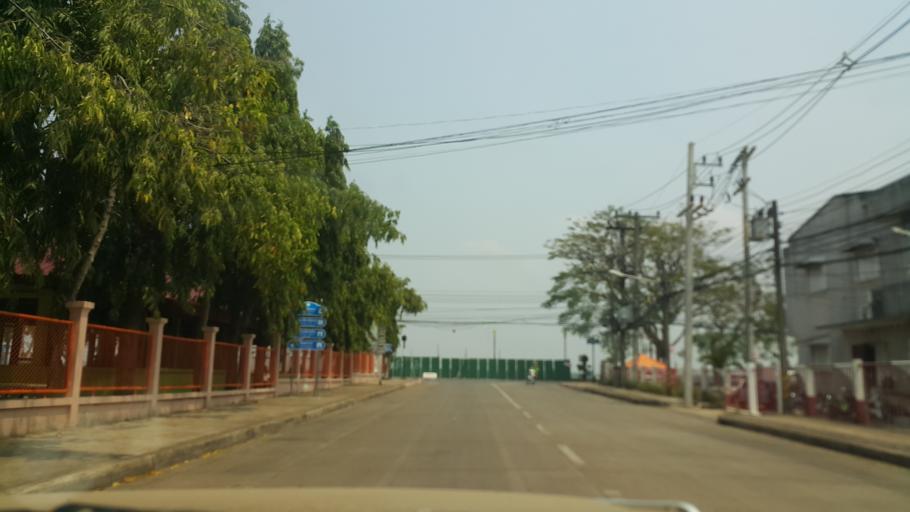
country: TH
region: Nakhon Phanom
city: Nakhon Phanom
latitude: 17.4079
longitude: 104.7849
